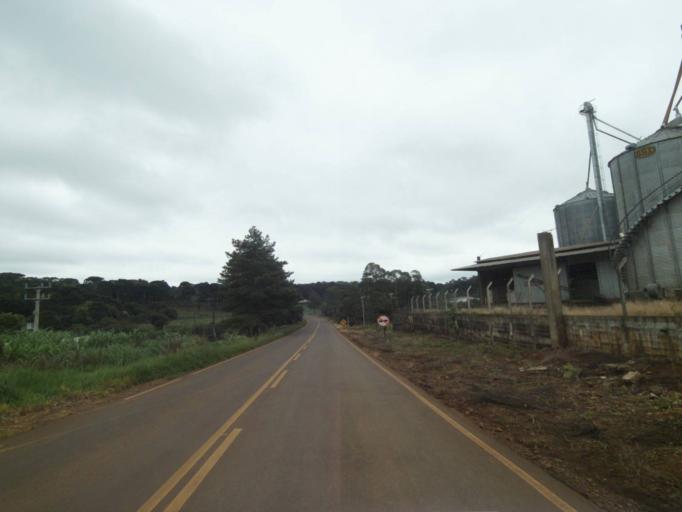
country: BR
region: Parana
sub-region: Pitanga
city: Pitanga
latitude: -24.9325
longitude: -51.8800
